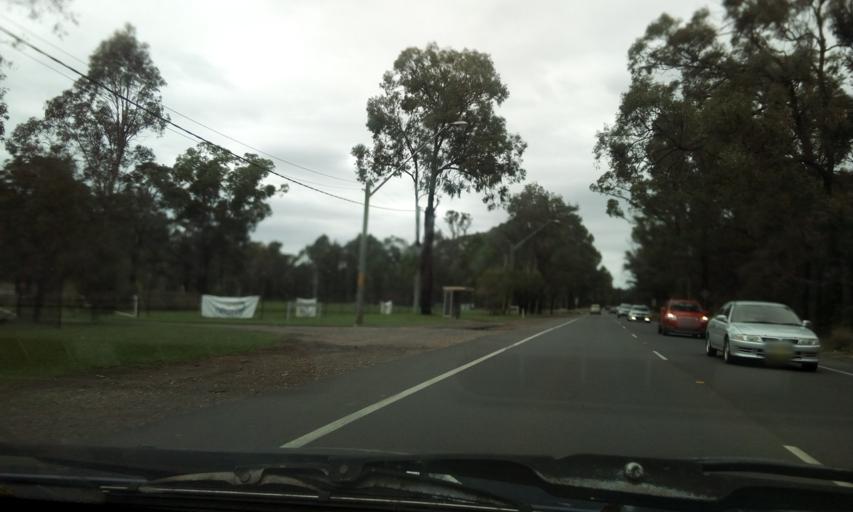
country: AU
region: New South Wales
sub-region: Penrith Municipality
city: Werrington Downs
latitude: -33.6986
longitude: 150.7270
